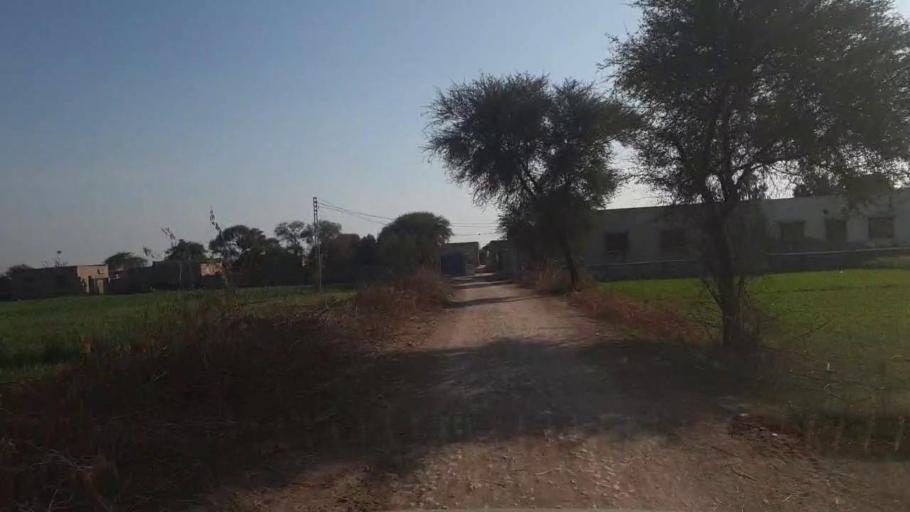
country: PK
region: Sindh
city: Chambar
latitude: 25.2909
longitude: 68.8626
